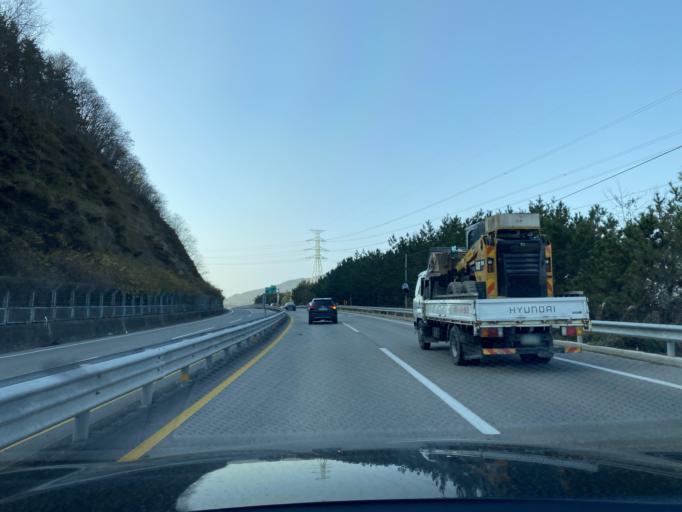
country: KR
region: Chungcheongnam-do
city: Hongsung
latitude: 36.6866
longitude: 126.6633
